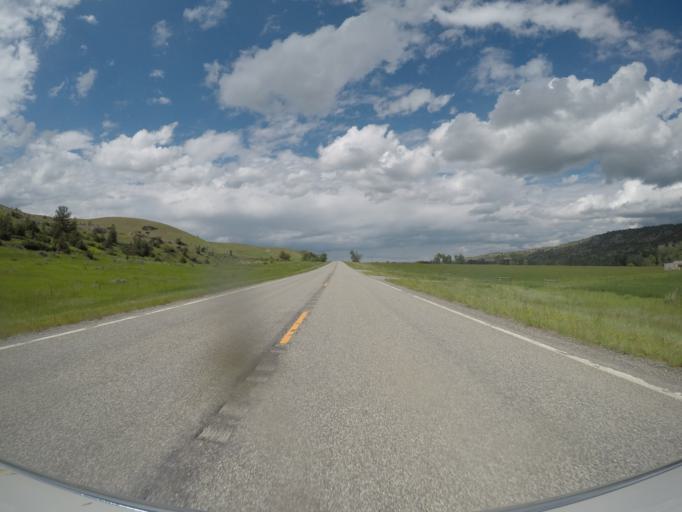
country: US
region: Montana
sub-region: Sweet Grass County
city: Big Timber
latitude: 45.7427
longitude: -109.9963
